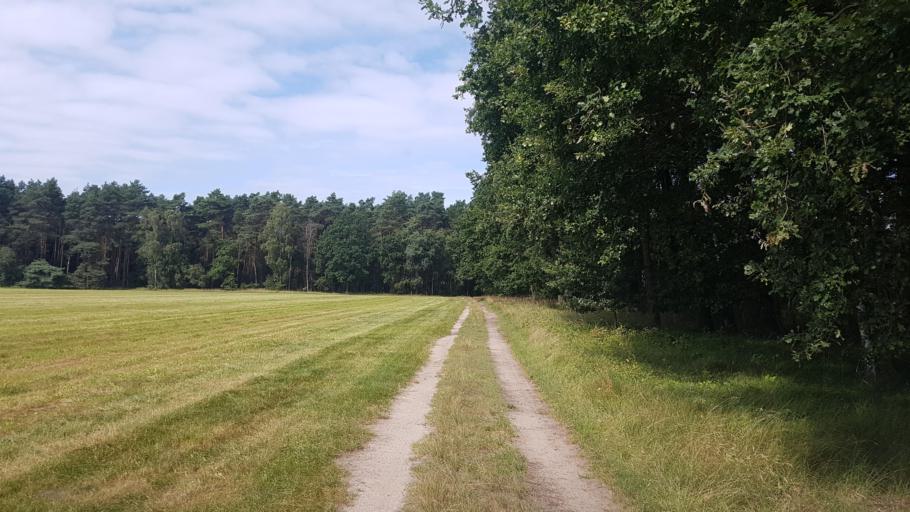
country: DE
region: Brandenburg
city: Bronkow
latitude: 51.6331
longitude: 13.8862
